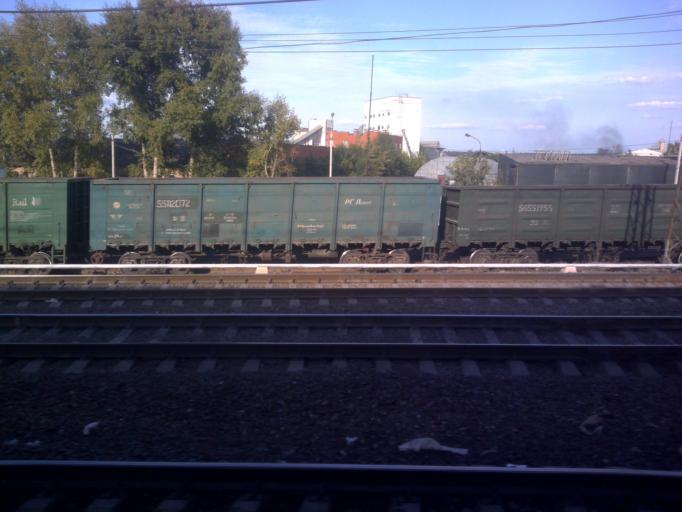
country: RU
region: Moskovskaya
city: Domodedovo
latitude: 55.4450
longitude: 37.7696
